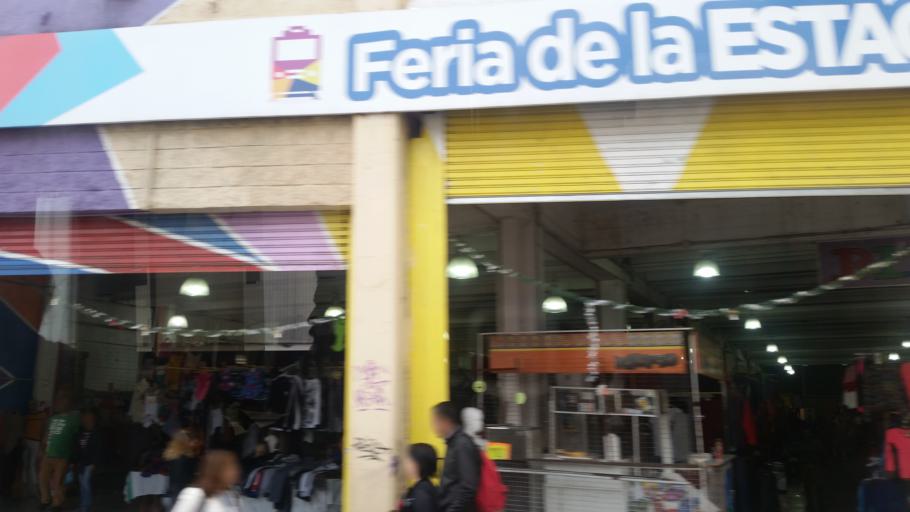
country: AR
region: Buenos Aires F.D.
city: Buenos Aires
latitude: -34.6078
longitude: -58.4072
